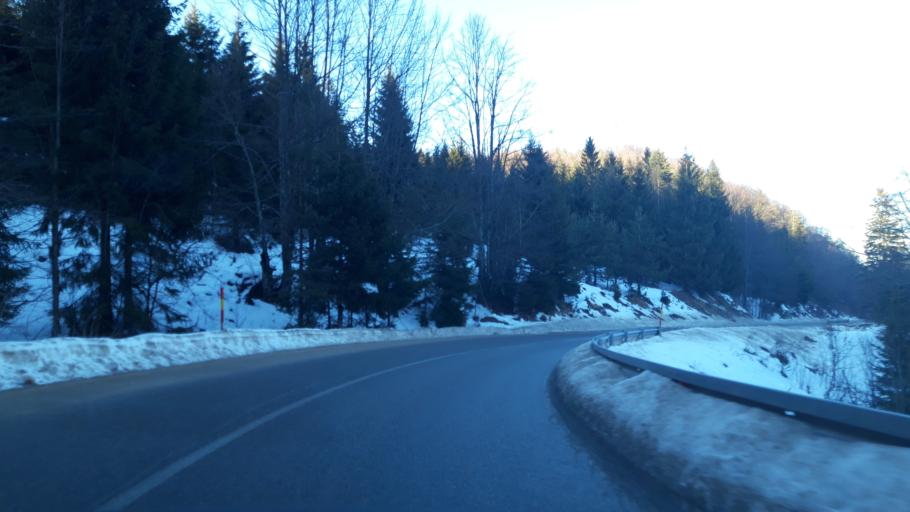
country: BA
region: Republika Srpska
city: Vlasenica
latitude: 44.1494
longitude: 18.9410
